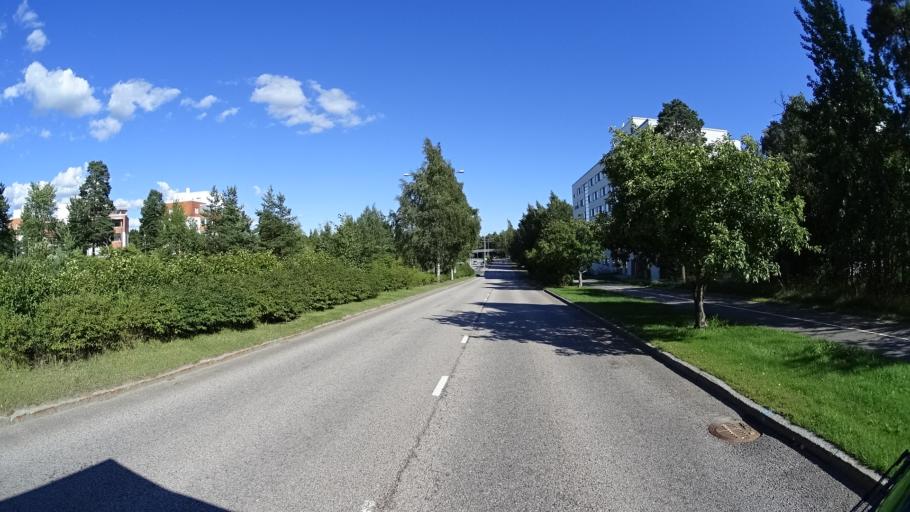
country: FI
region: Uusimaa
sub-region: Helsinki
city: Vantaa
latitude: 60.2374
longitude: 25.0950
